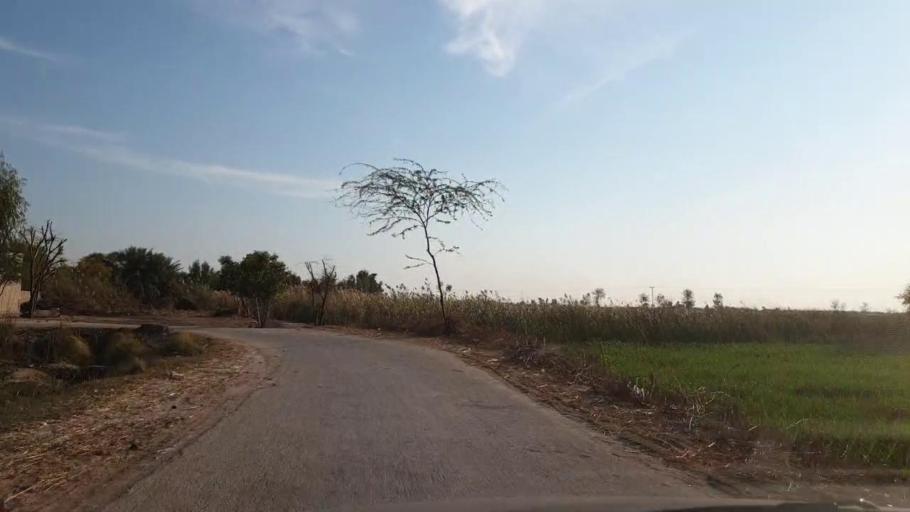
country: PK
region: Sindh
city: Khadro
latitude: 26.1899
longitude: 68.7471
